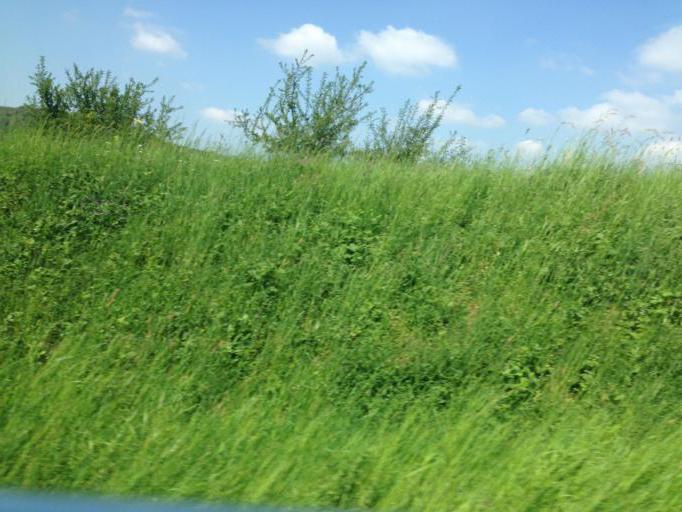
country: DE
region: North Rhine-Westphalia
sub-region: Regierungsbezirk Koln
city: Bad Munstereifel
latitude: 50.5481
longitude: 6.7342
